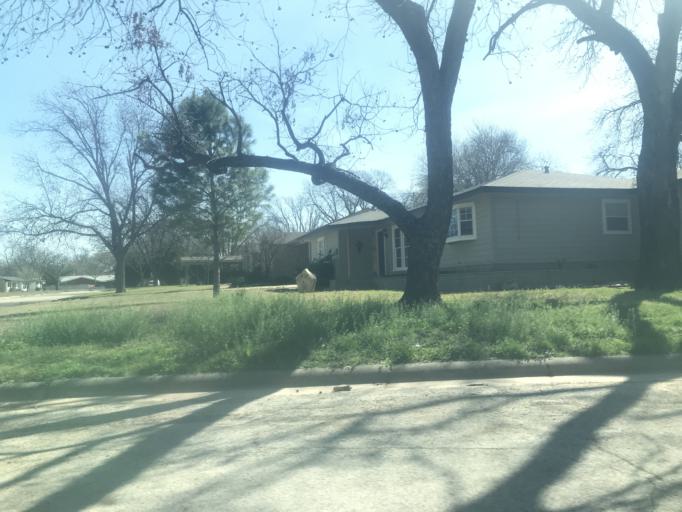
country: US
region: Texas
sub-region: Taylor County
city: Abilene
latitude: 32.4359
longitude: -99.7763
